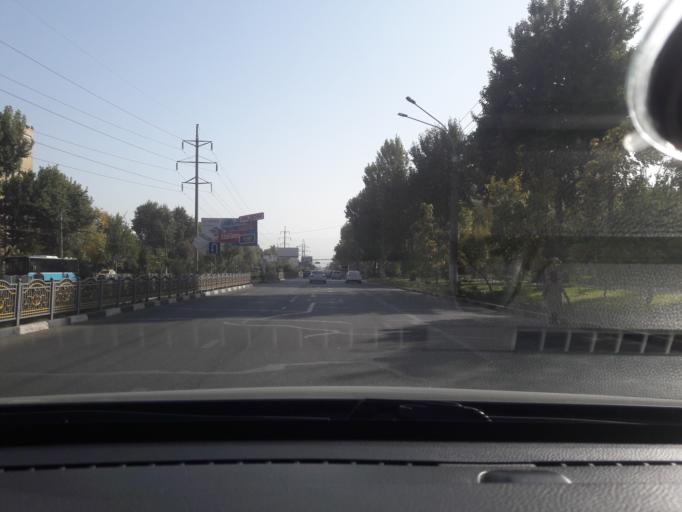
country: TJ
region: Dushanbe
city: Dushanbe
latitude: 38.5283
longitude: 68.7618
